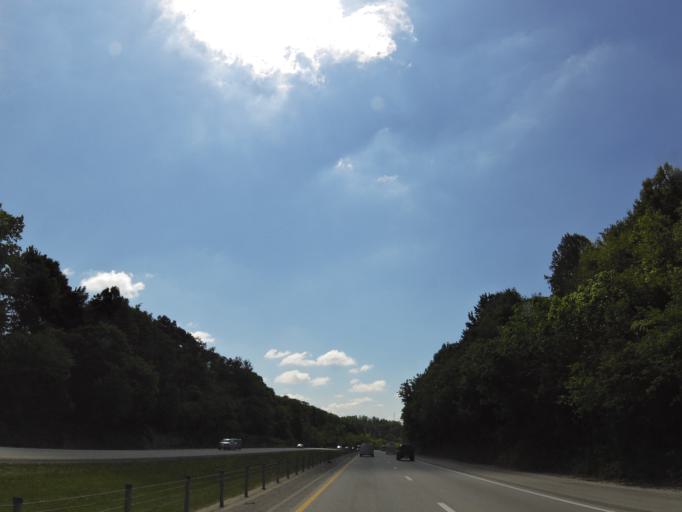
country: US
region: Kentucky
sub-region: Rockcastle County
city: Mount Vernon
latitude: 37.3032
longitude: -84.2828
